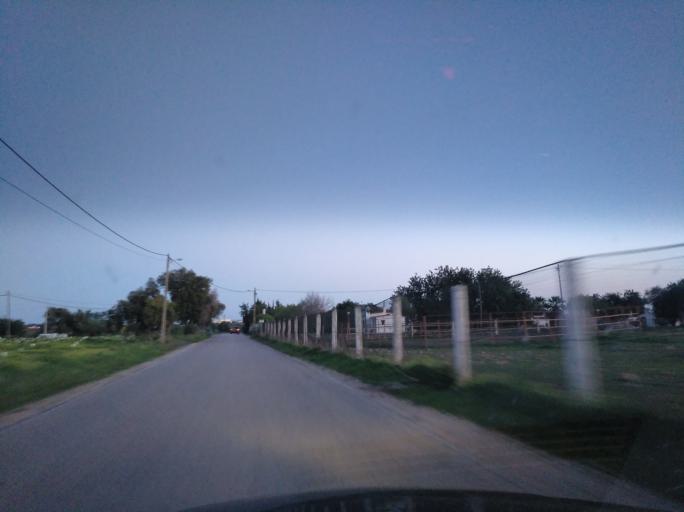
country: PT
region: Faro
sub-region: Vila Real de Santo Antonio
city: Monte Gordo
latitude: 37.1861
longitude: -7.5085
